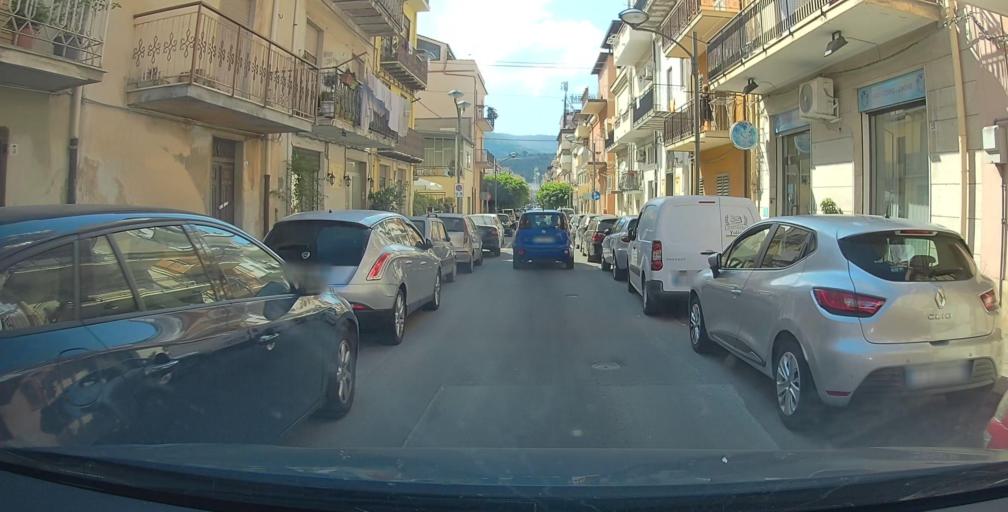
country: IT
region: Sicily
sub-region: Messina
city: Patti
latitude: 38.1513
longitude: 14.9712
